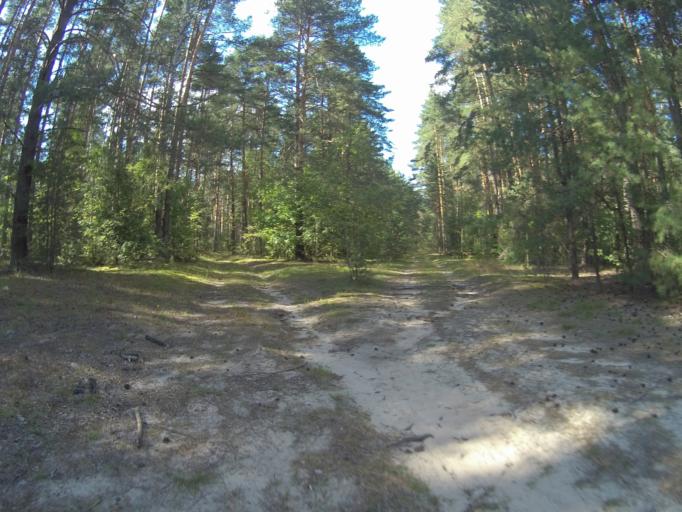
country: RU
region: Vladimir
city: Kommunar
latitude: 56.0515
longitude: 40.4602
